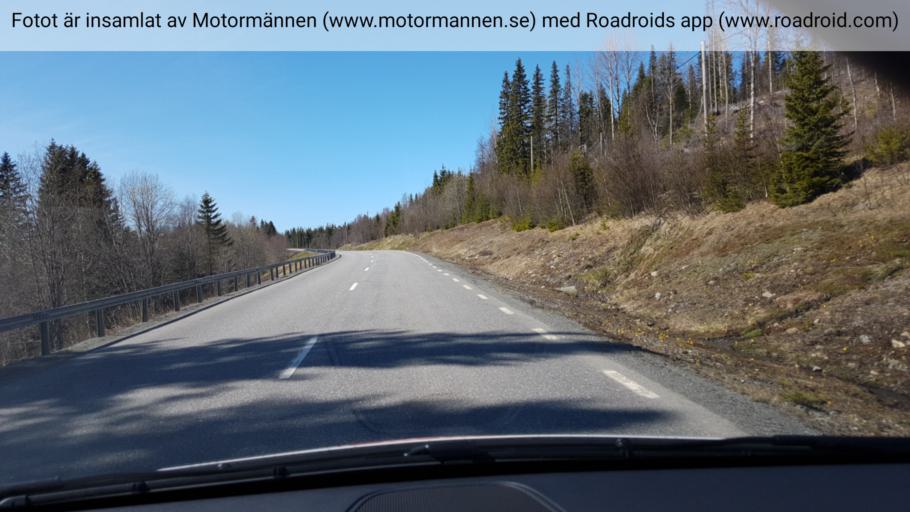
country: SE
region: Jaemtland
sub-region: Are Kommun
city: Are
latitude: 63.6167
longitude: 13.1982
